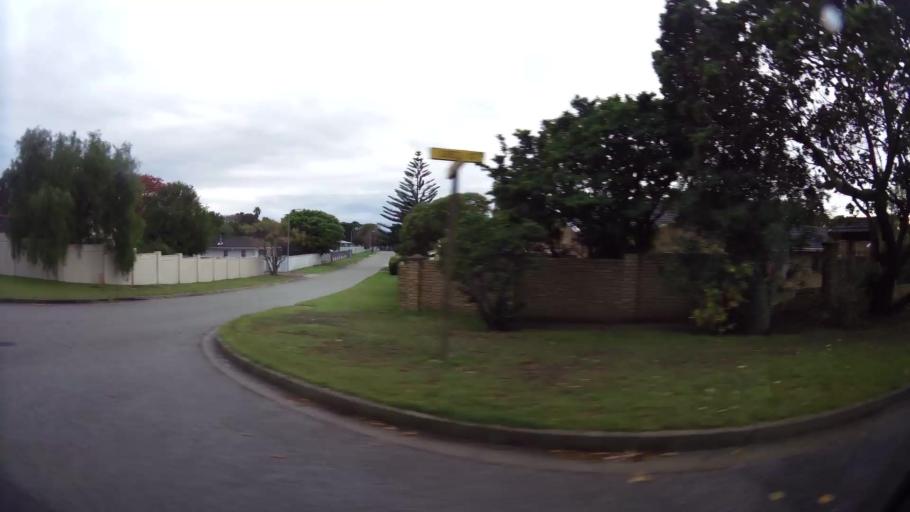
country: ZA
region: Eastern Cape
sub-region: Nelson Mandela Bay Metropolitan Municipality
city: Port Elizabeth
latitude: -33.9952
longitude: 25.5604
